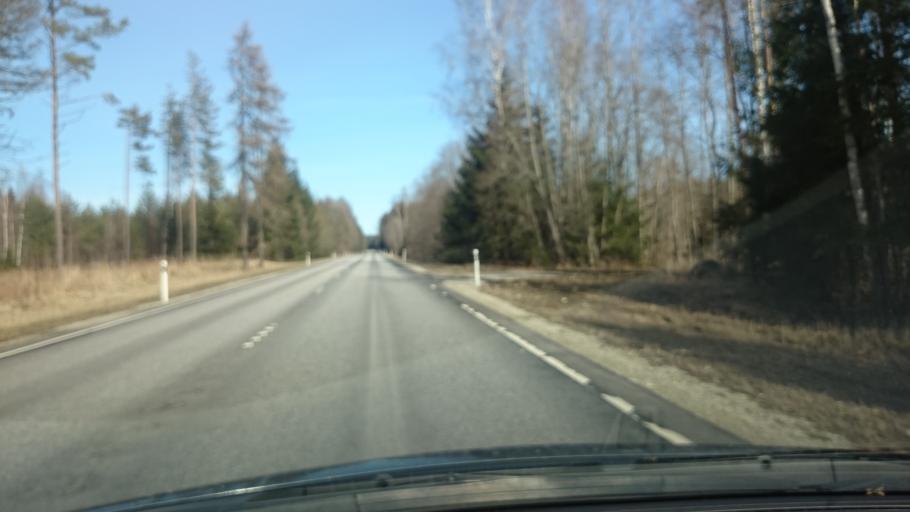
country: EE
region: Jaervamaa
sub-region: Tueri vald
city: Sarevere
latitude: 58.6899
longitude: 25.2461
